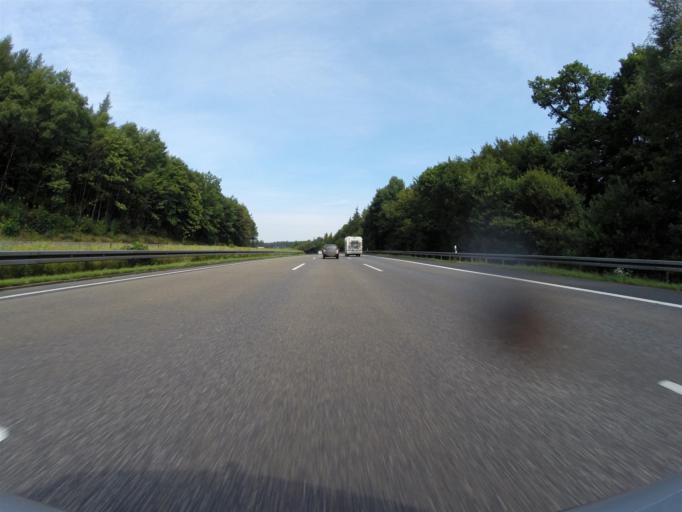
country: DE
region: Hesse
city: Schwarzenborn
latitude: 50.9564
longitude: 9.5014
